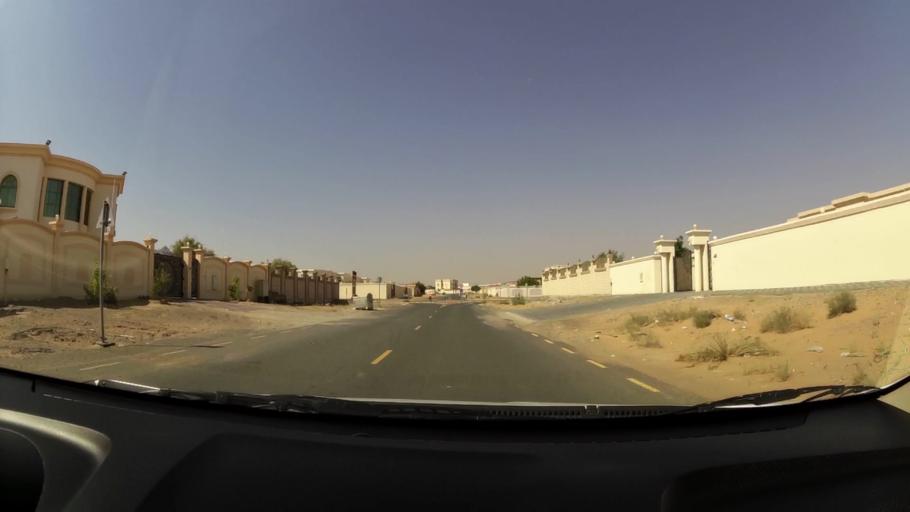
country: AE
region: Umm al Qaywayn
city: Umm al Qaywayn
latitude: 25.4714
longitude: 55.6146
